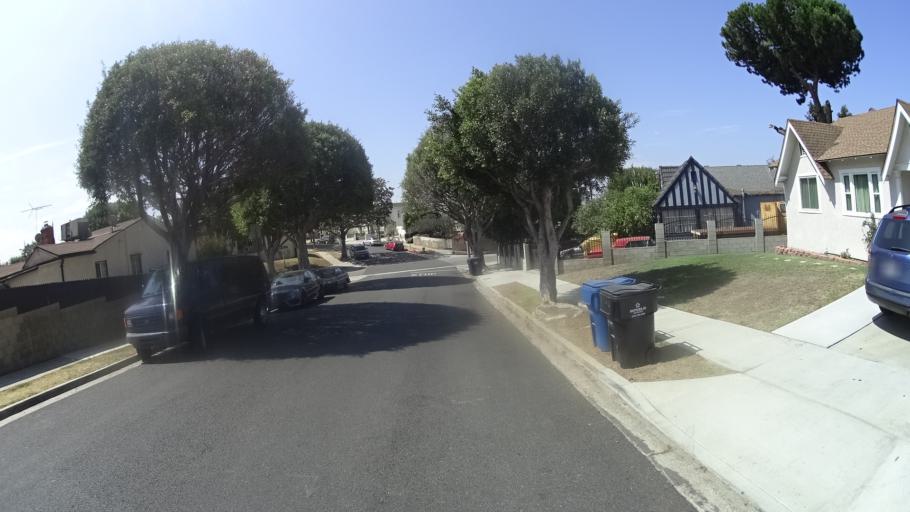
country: US
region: California
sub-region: Los Angeles County
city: Inglewood
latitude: 33.9779
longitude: -118.3558
